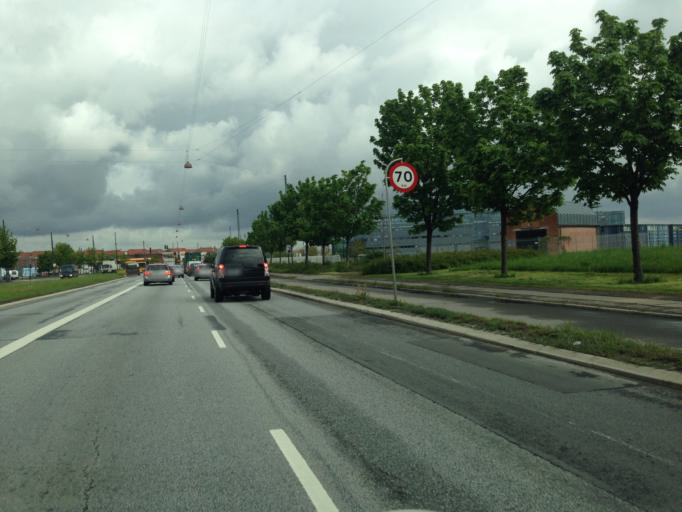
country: DK
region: Capital Region
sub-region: Frederiksberg Kommune
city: Frederiksberg
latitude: 55.6449
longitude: 12.5439
